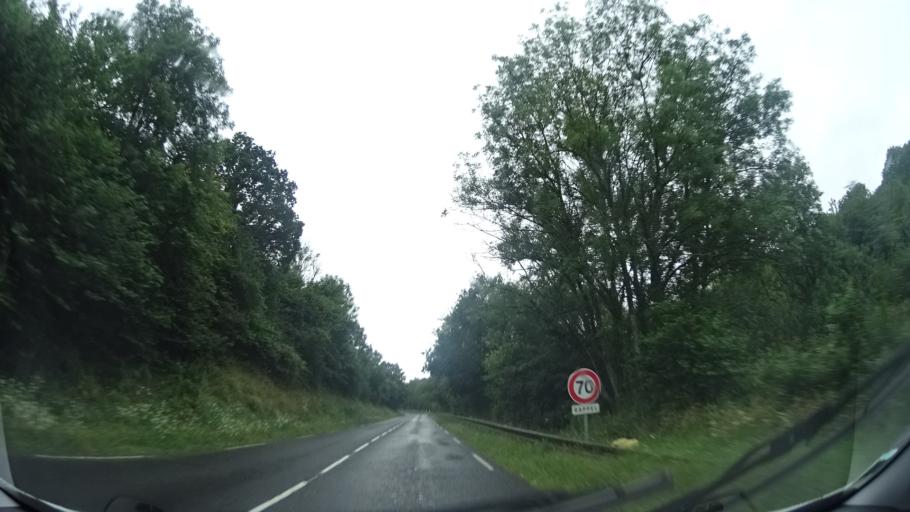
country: FR
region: Lower Normandy
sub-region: Departement de la Manche
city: Beaumont-Hague
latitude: 49.6105
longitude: -1.7900
